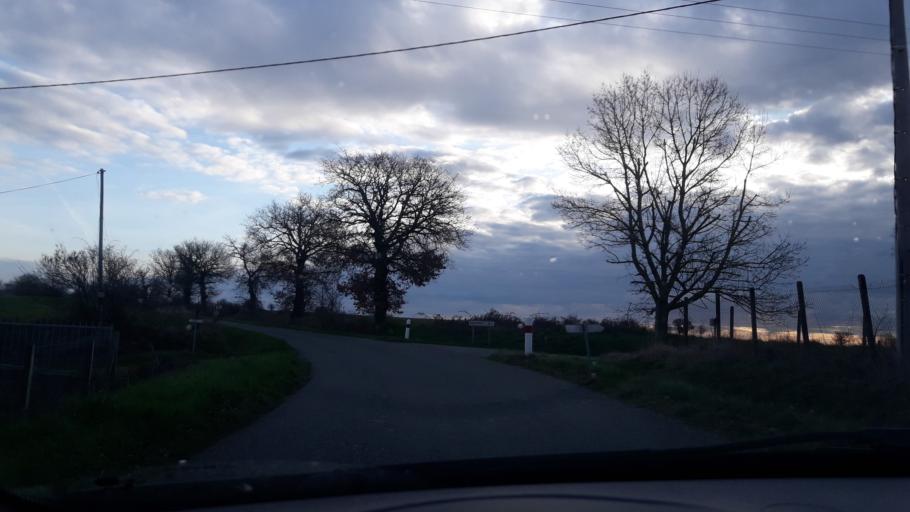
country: FR
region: Midi-Pyrenees
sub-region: Departement du Gers
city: Gimont
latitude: 43.6468
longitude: 1.0016
